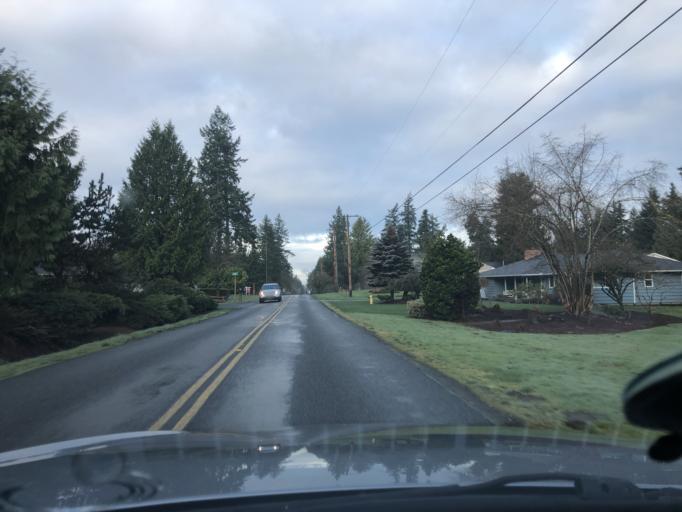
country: US
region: Washington
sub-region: Pierce County
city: Edgewood
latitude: 47.2428
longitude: -122.2971
